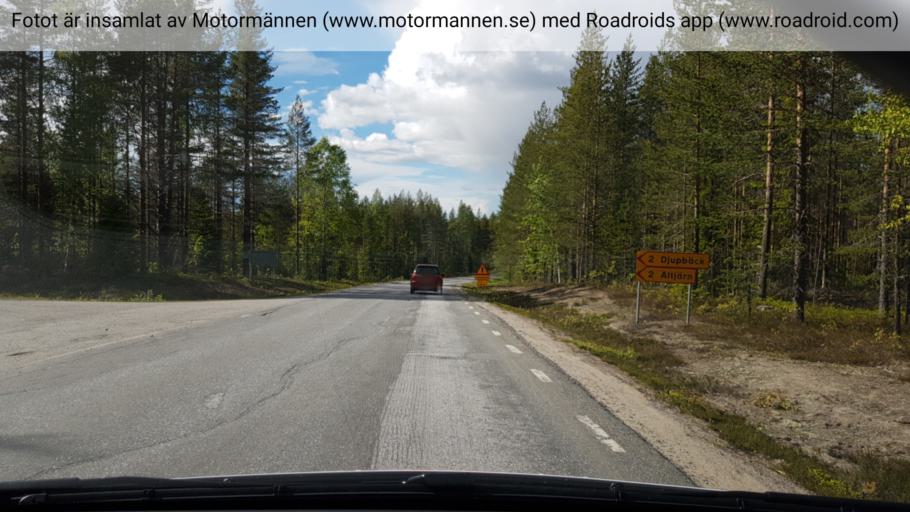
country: SE
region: Vaesterbotten
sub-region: Vannas Kommun
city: Vannasby
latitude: 64.0657
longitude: 19.9908
